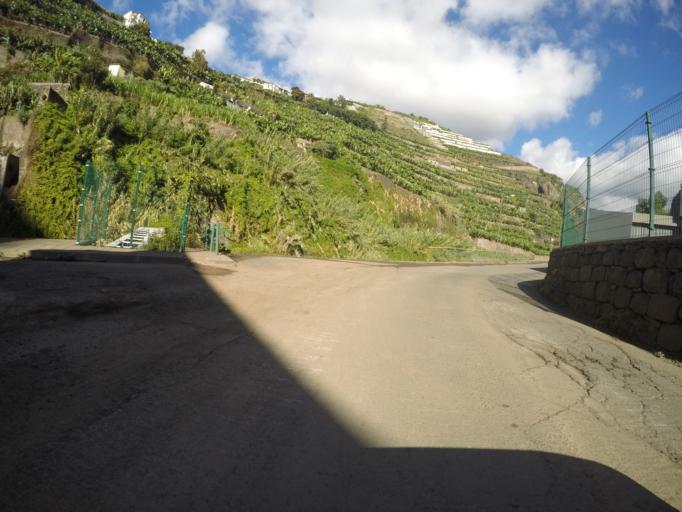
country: PT
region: Madeira
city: Camara de Lobos
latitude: 32.6557
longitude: -16.9644
